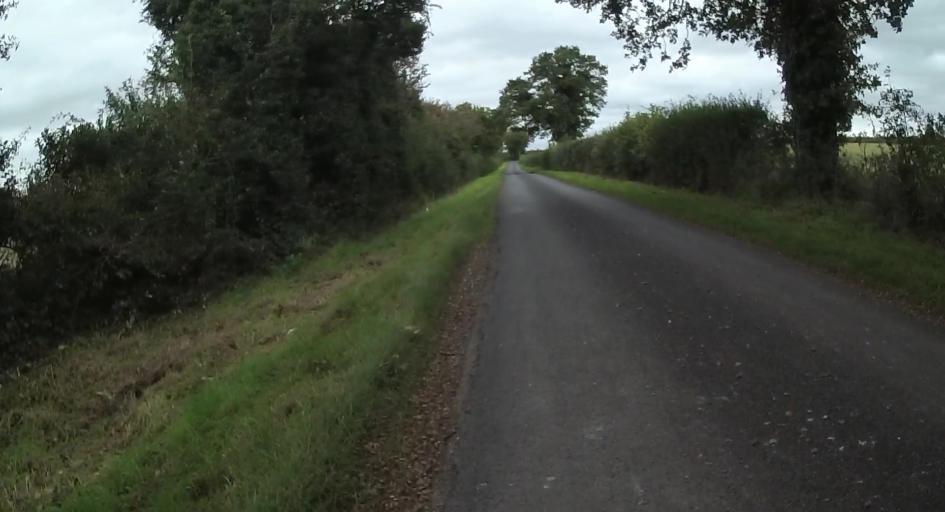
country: GB
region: England
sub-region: Hampshire
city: Four Marks
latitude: 51.1549
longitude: -1.1174
